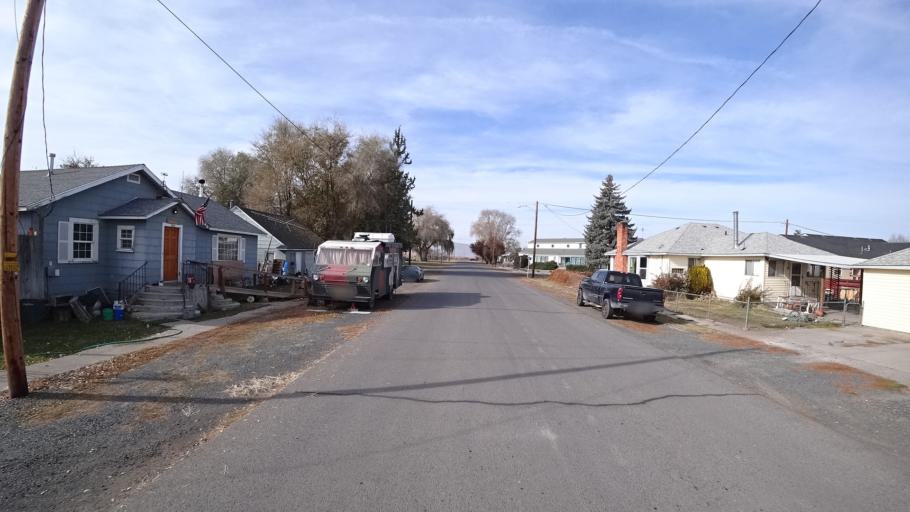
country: US
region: California
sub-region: Siskiyou County
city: Tulelake
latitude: 41.9573
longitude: -121.4786
